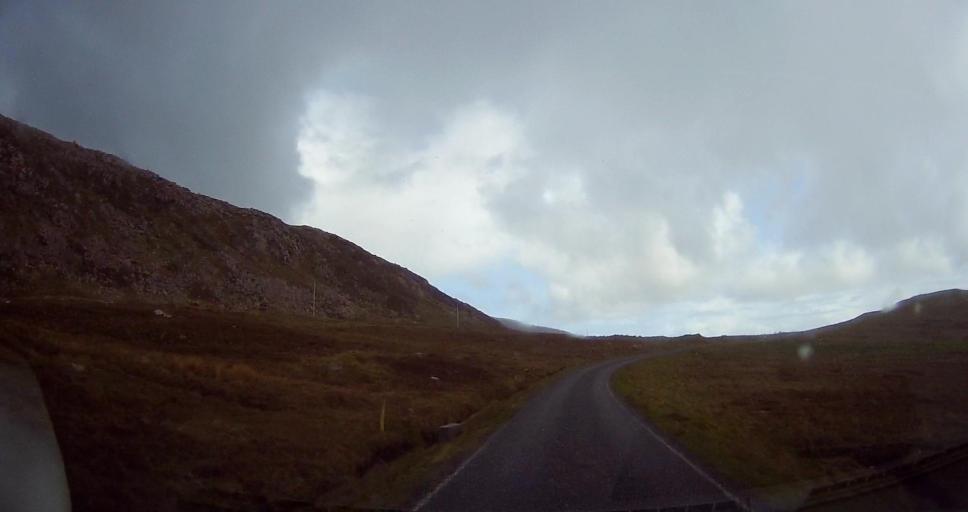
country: GB
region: Scotland
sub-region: Shetland Islands
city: Lerwick
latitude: 60.5510
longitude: -1.3408
